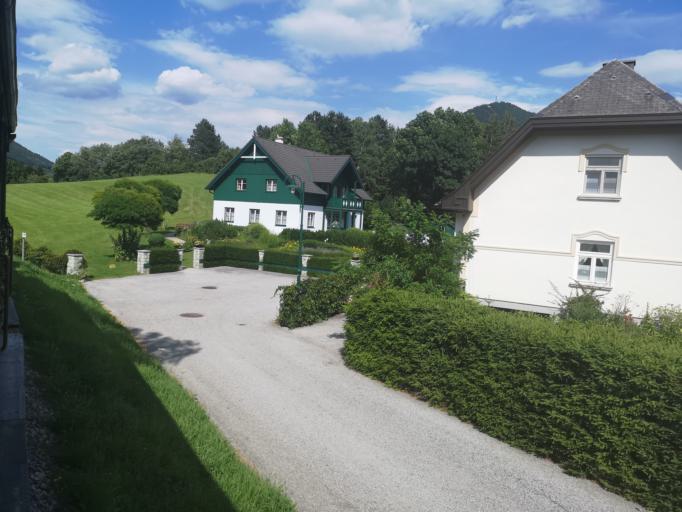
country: AT
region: Lower Austria
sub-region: Politischer Bezirk Neunkirchen
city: Puchberg am Schneeberg
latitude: 47.7874
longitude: 15.9019
